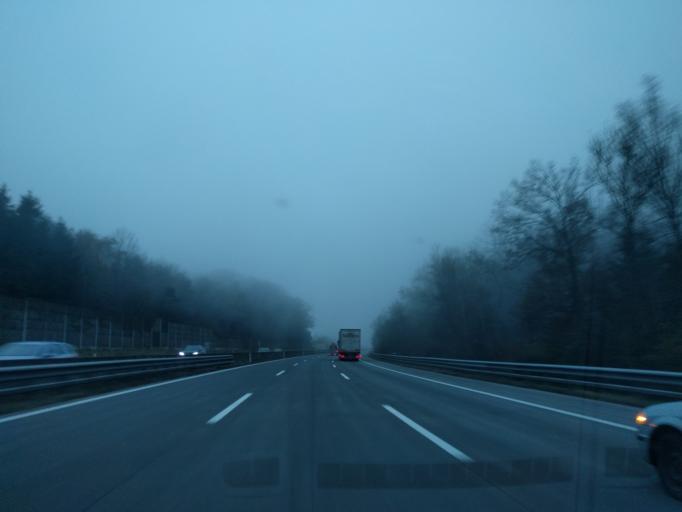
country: AT
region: Lower Austria
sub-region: Politischer Bezirk Amstetten
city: Zeillern
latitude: 48.1203
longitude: 14.8061
